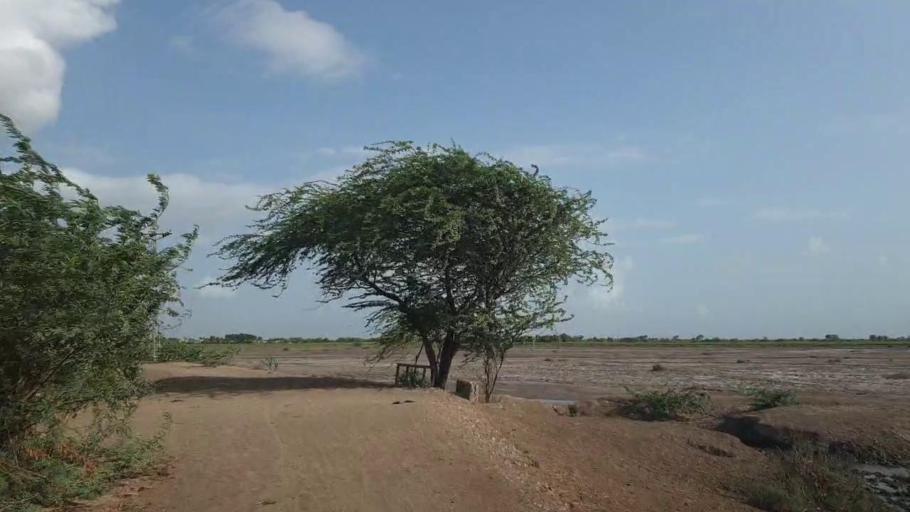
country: PK
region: Sindh
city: Kadhan
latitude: 24.6301
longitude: 69.0813
